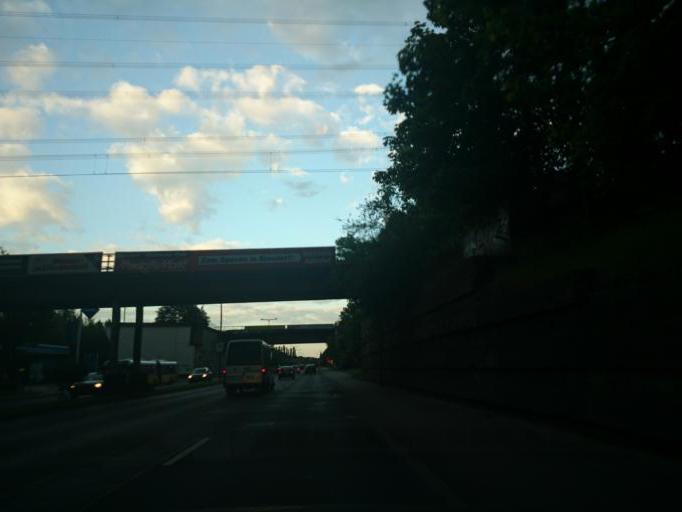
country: DE
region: Berlin
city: Biesdorf
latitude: 52.5100
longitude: 13.5375
